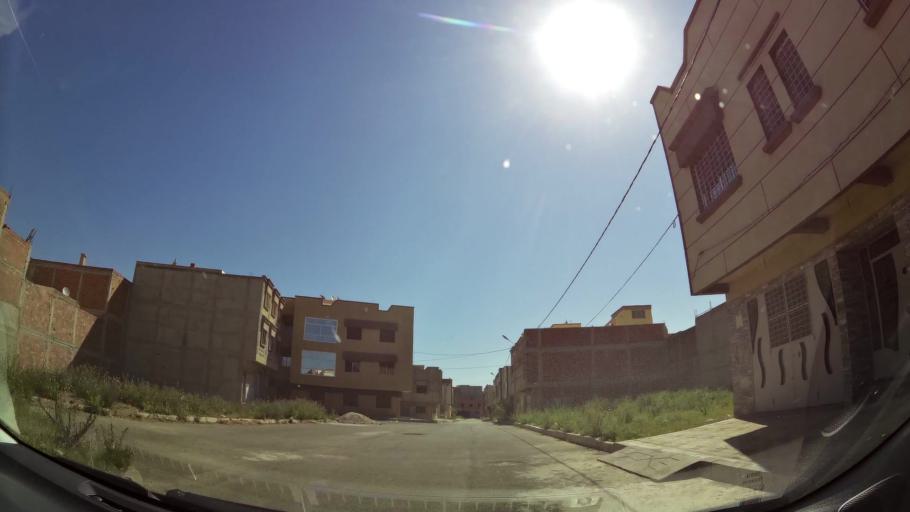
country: MA
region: Oriental
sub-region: Oujda-Angad
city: Oujda
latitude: 34.6523
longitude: -1.8855
